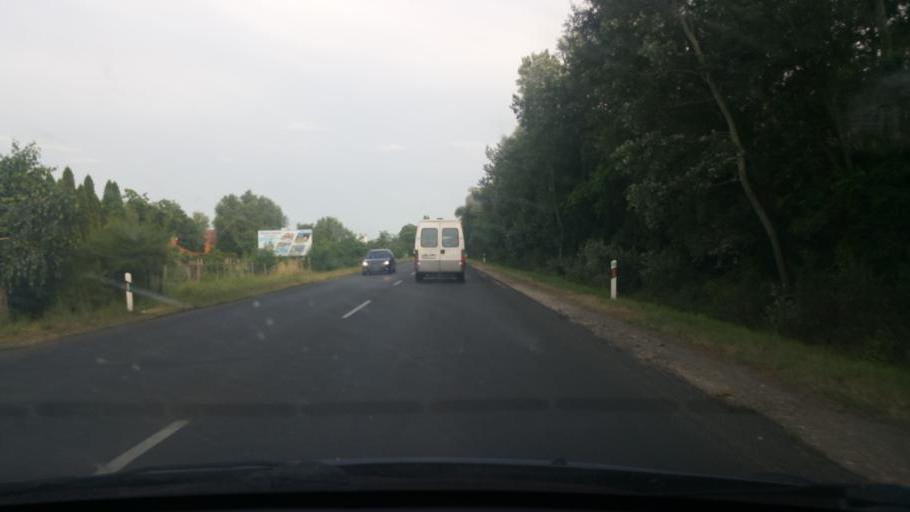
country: HU
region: Pest
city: Monor
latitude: 47.3382
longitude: 19.4331
